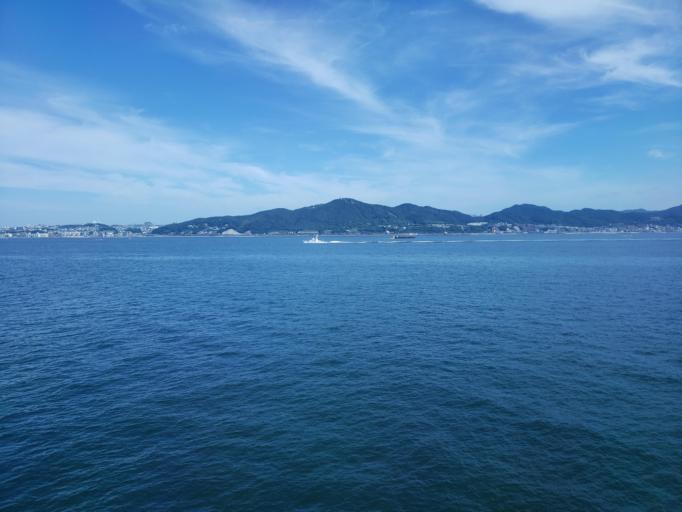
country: JP
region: Hyogo
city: Kobe
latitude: 34.6103
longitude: 135.1087
